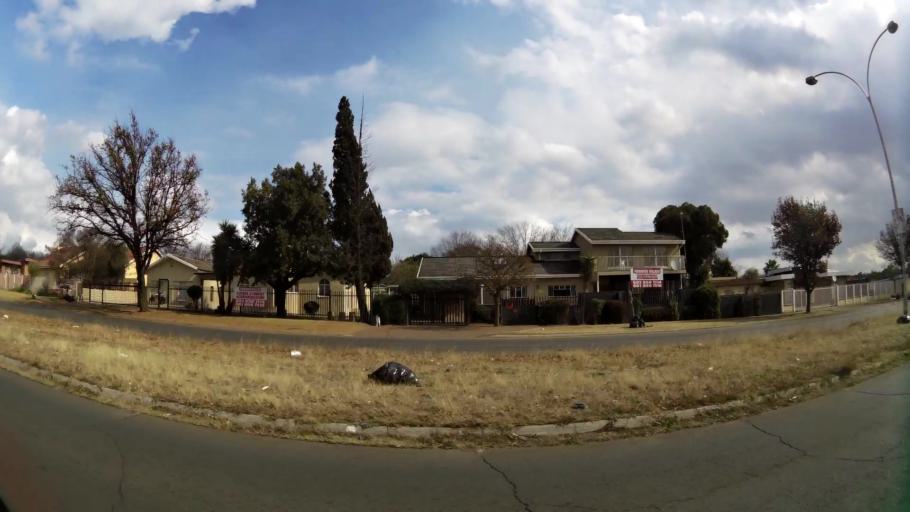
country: ZA
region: Gauteng
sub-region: Sedibeng District Municipality
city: Vanderbijlpark
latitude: -26.7138
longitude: 27.8623
